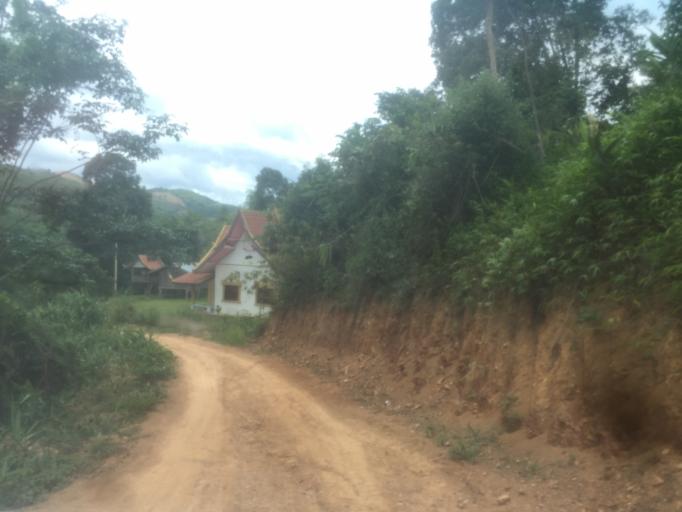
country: LA
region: Phongsali
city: Khoa
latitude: 20.9145
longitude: 102.5609
